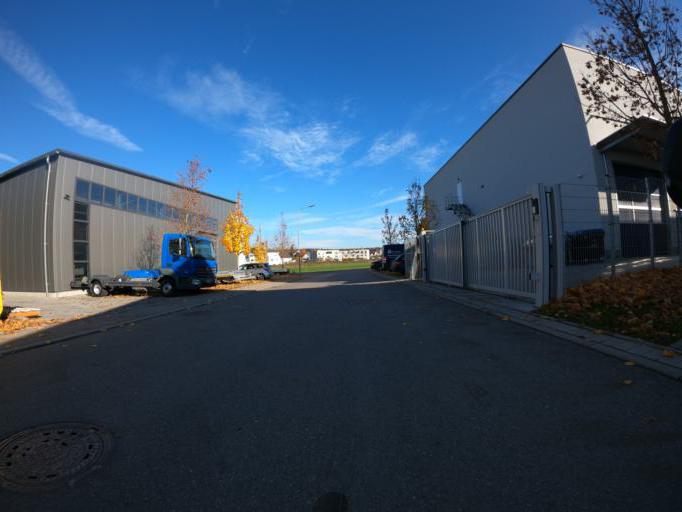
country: DE
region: Baden-Wuerttemberg
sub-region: Regierungsbezirk Stuttgart
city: Magstadt
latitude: 48.7348
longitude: 8.9741
